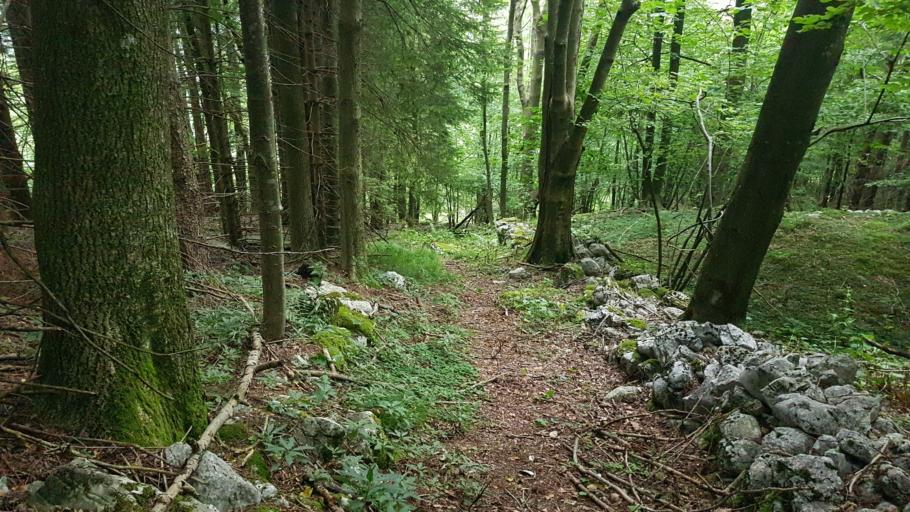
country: IT
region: Friuli Venezia Giulia
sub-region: Provincia di Udine
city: Lusevera
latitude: 46.3029
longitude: 13.2827
